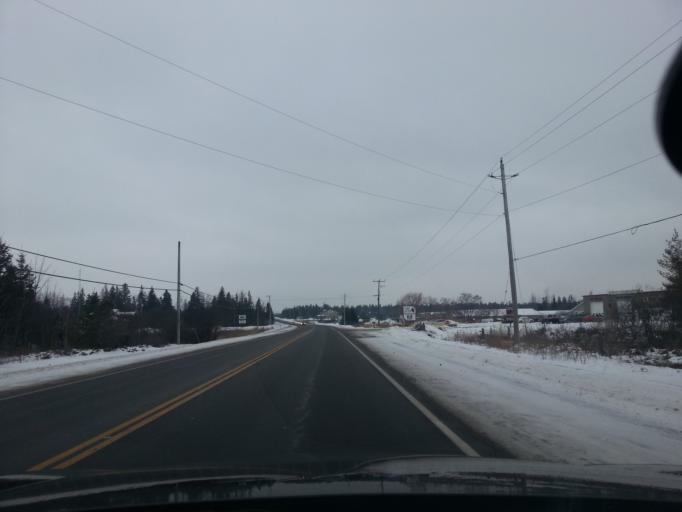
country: CA
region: Ontario
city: Carleton Place
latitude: 45.2528
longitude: -76.1559
